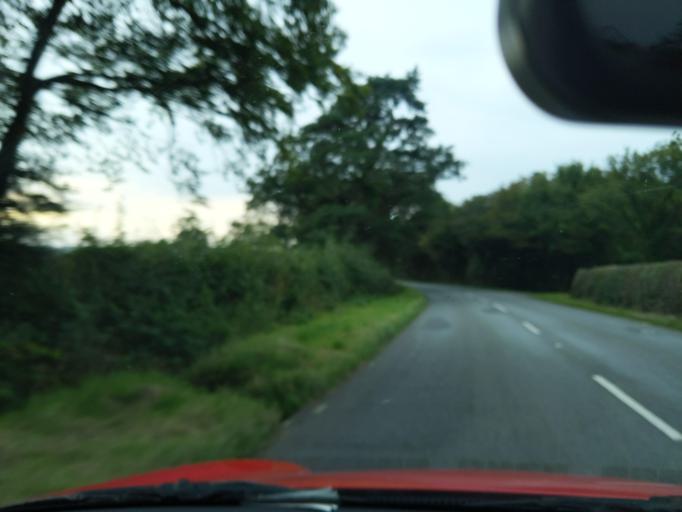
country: GB
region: England
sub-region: Devon
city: Okehampton
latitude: 50.7967
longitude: -4.0431
